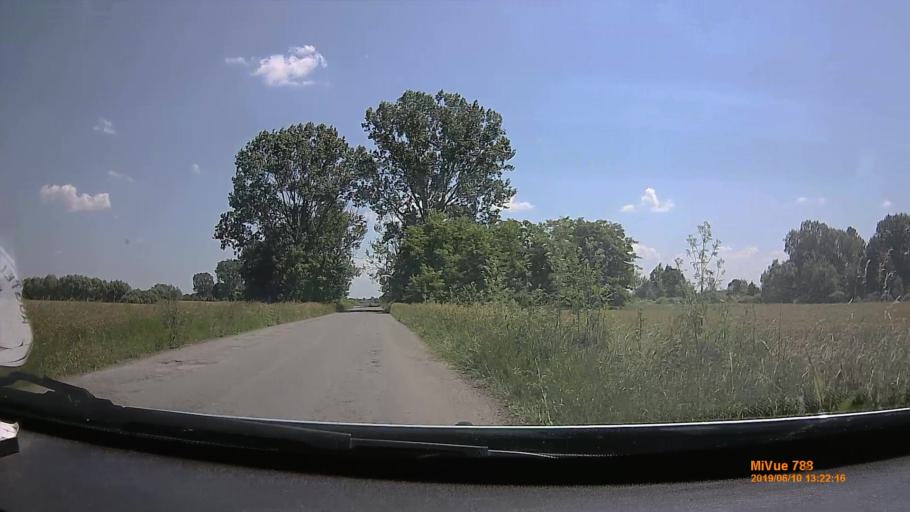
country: HU
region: Borsod-Abauj-Zemplen
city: Tiszaluc
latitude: 48.0309
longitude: 21.0812
